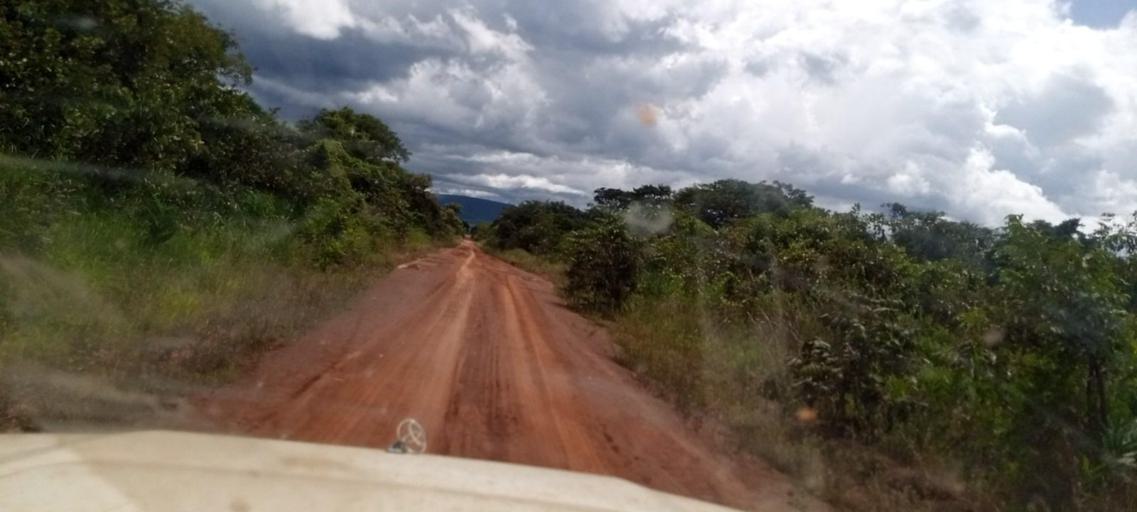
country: ZM
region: Luapula
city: Mwense
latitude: -10.1834
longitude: 28.1221
